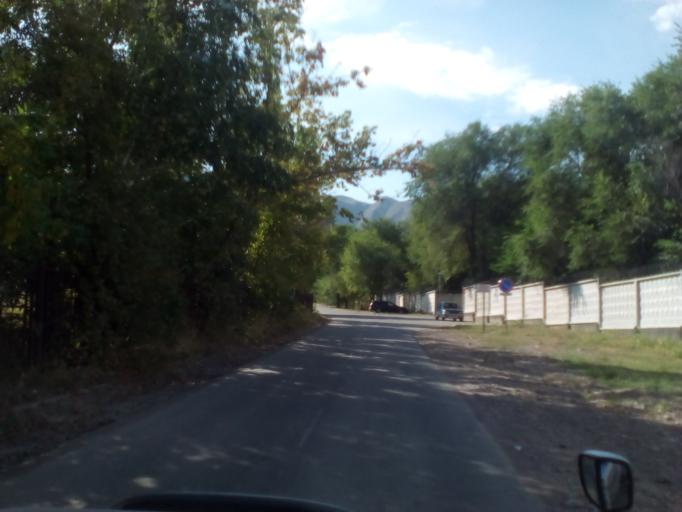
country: KZ
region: Almaty Oblysy
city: Burunday
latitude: 43.1602
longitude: 76.3823
